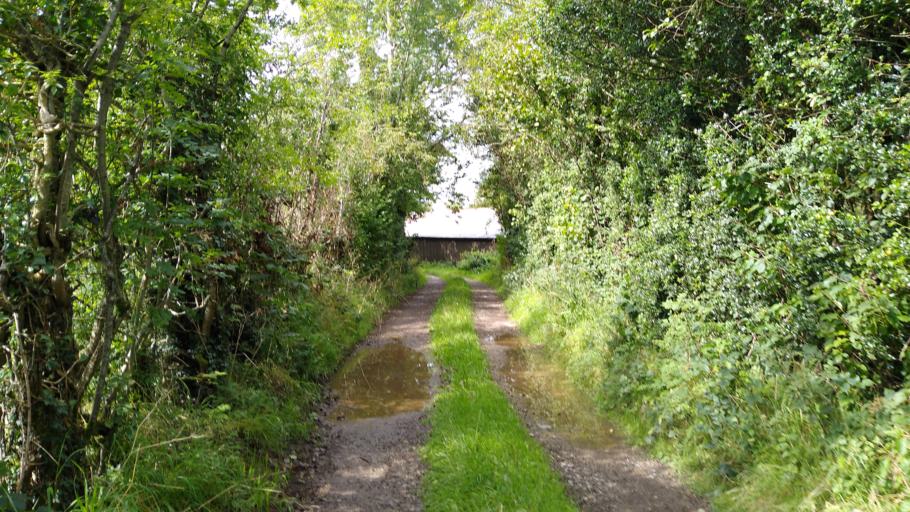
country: GB
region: England
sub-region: Cumbria
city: Cockermouth
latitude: 54.6370
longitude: -3.3376
